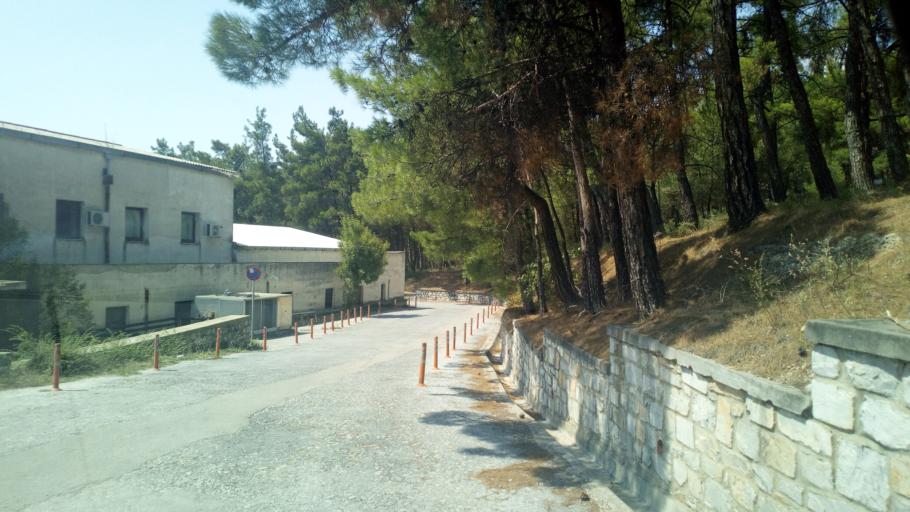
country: GR
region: Central Macedonia
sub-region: Nomos Thessalonikis
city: Asvestochori
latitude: 40.6318
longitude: 23.0462
